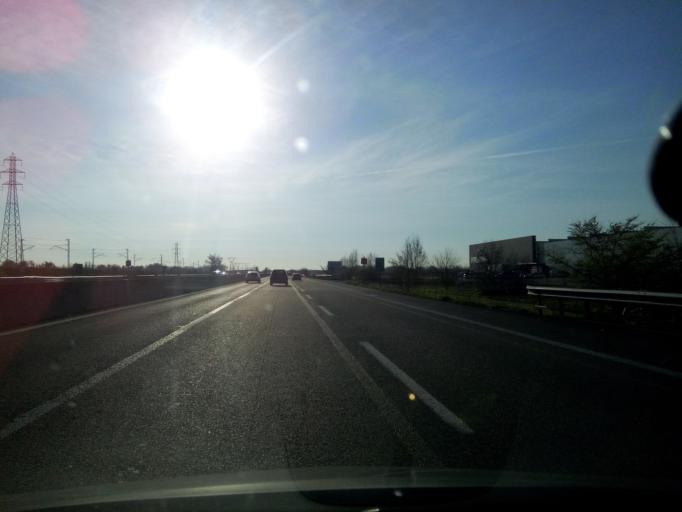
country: IT
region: Emilia-Romagna
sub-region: Provincia di Parma
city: Baganzola
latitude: 44.8511
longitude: 10.2922
